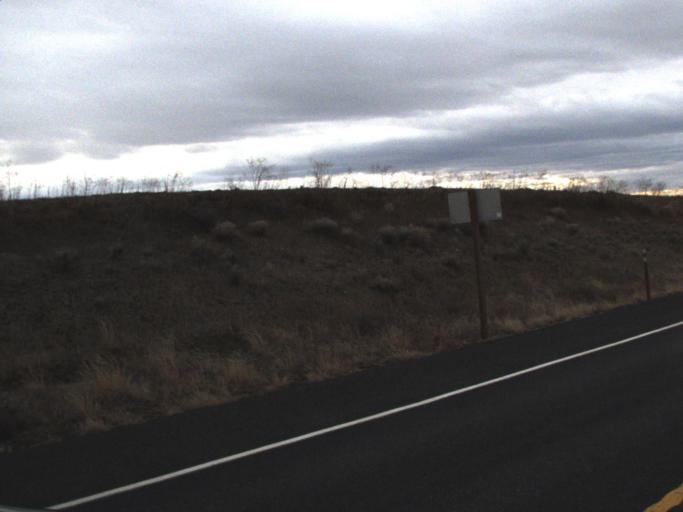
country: US
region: Washington
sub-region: Adams County
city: Ritzville
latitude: 46.7955
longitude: -118.4842
